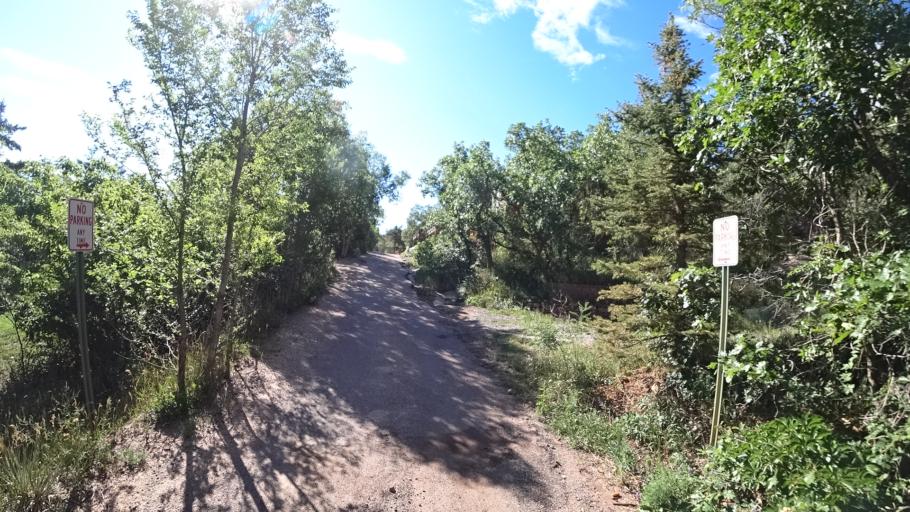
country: US
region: Colorado
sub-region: El Paso County
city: Manitou Springs
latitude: 38.8545
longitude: -104.9183
